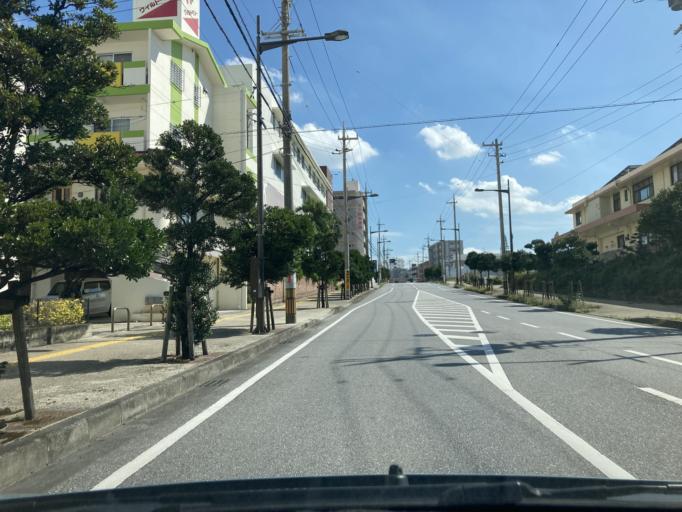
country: JP
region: Okinawa
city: Ginowan
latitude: 26.2728
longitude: 127.7303
